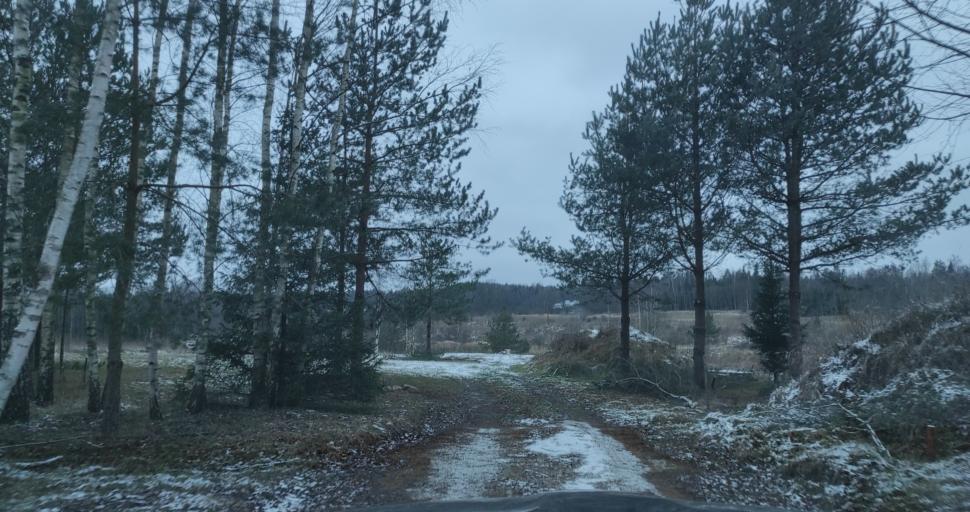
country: LV
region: Kuldigas Rajons
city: Kuldiga
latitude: 56.9799
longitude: 22.0512
